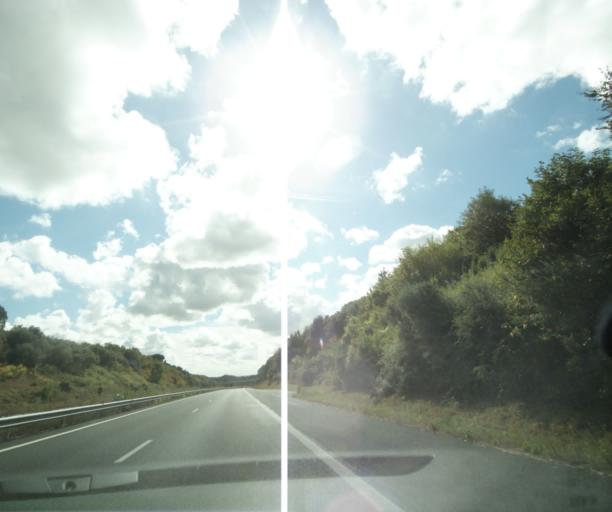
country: FR
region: Poitou-Charentes
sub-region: Departement de la Charente-Maritime
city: Bords
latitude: 45.9001
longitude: -0.7590
